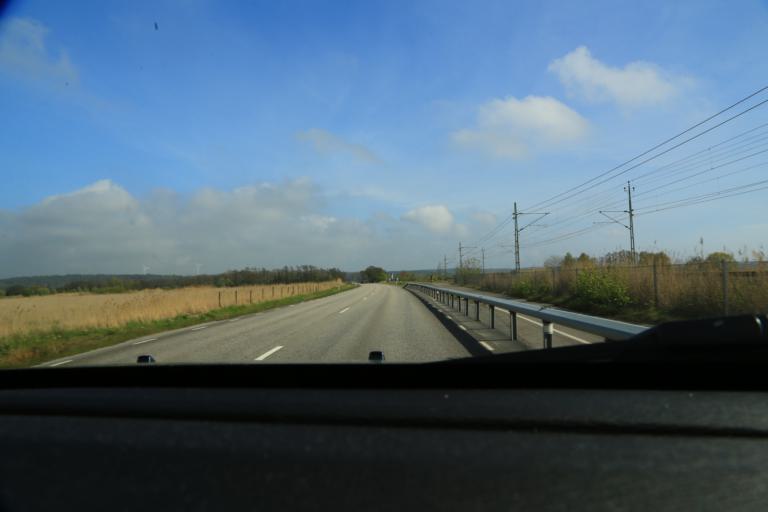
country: SE
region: Halland
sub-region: Kungsbacka Kommun
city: Frillesas
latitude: 57.2305
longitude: 12.2088
